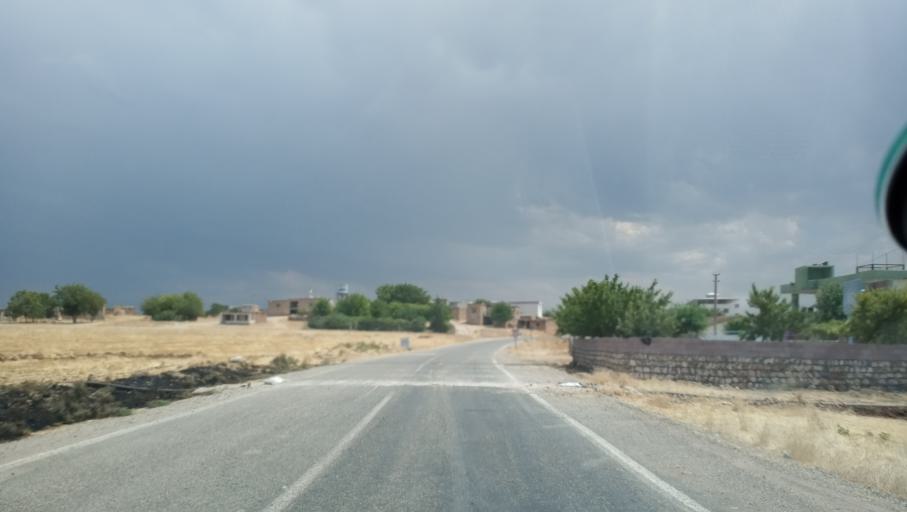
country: TR
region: Mardin
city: Baskavak
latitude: 37.6823
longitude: 40.8469
